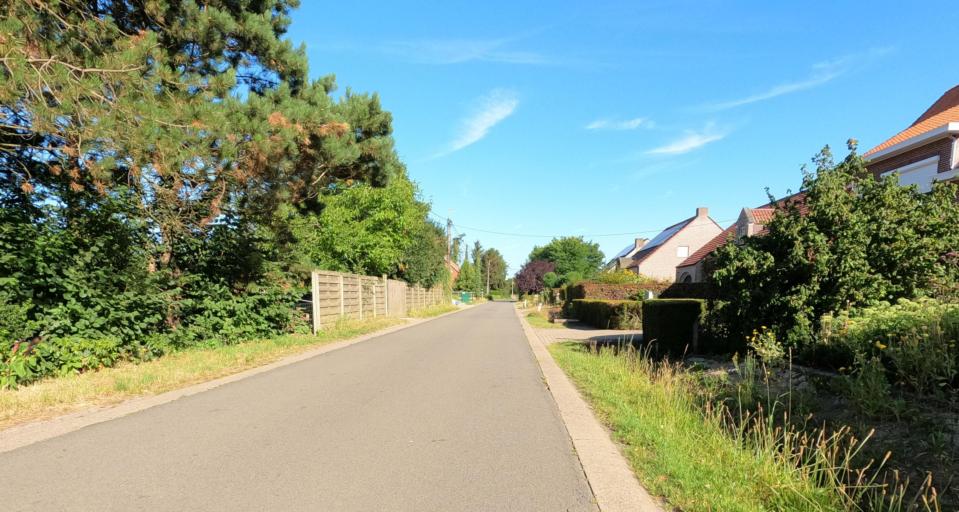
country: BE
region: Flanders
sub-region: Provincie Antwerpen
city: Grobbendonk
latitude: 51.1606
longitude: 4.7335
